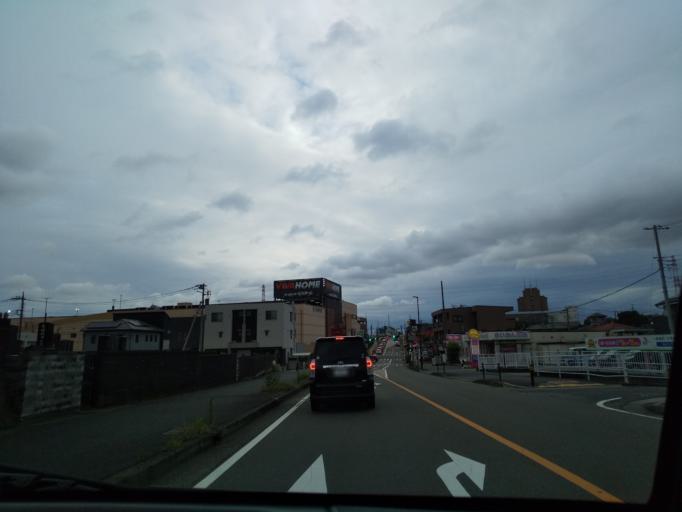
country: JP
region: Kanagawa
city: Minami-rinkan
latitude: 35.4386
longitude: 139.4311
